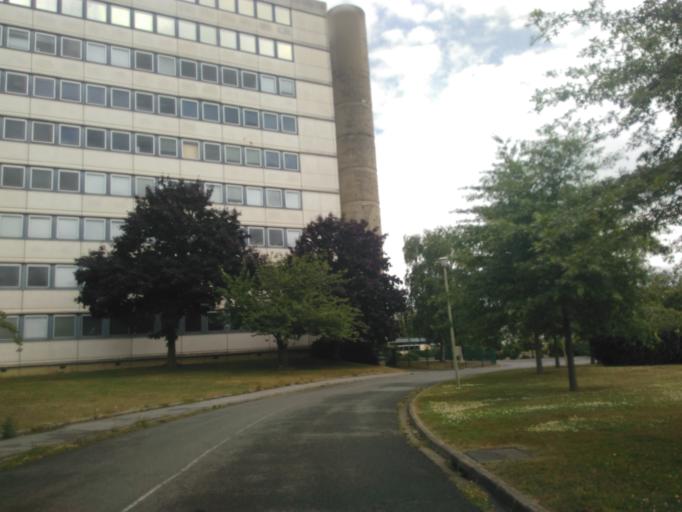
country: FR
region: Brittany
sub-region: Departement d'Ille-et-Vilaine
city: Rennes
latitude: 48.1189
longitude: -1.6426
